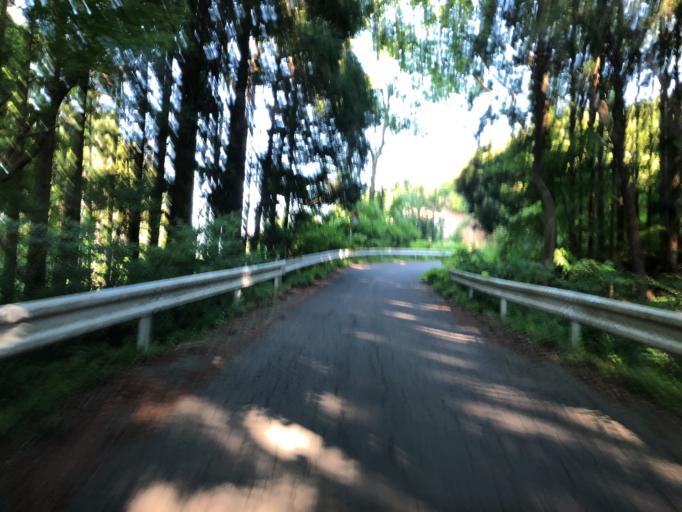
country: JP
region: Ibaraki
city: Kitaibaraki
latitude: 36.8687
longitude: 140.6777
